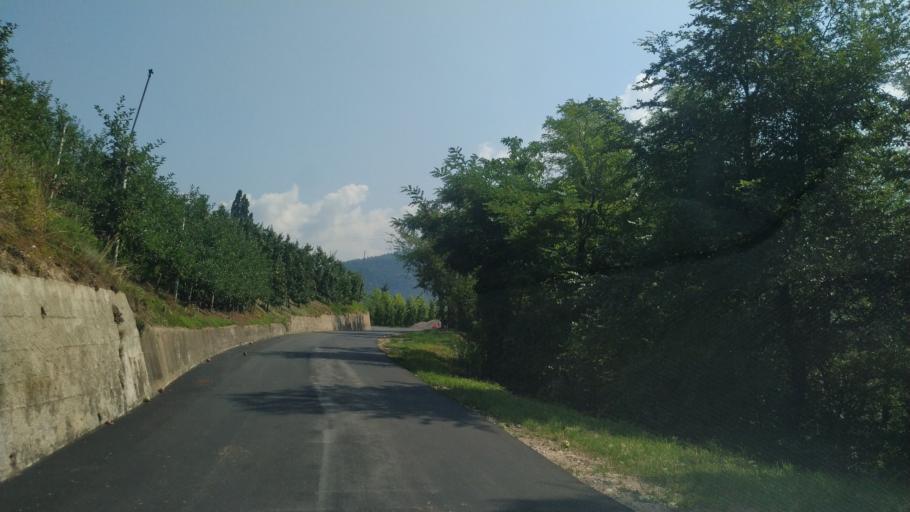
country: IT
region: Trentino-Alto Adige
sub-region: Provincia di Trento
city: Vigo di Ton
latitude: 46.2739
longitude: 11.0755
